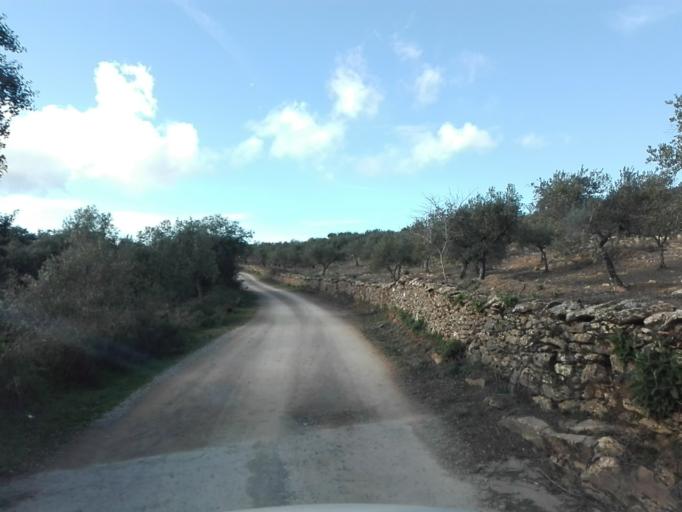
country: ES
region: Extremadura
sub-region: Provincia de Badajoz
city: Trasierra
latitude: 38.1964
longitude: -5.9873
